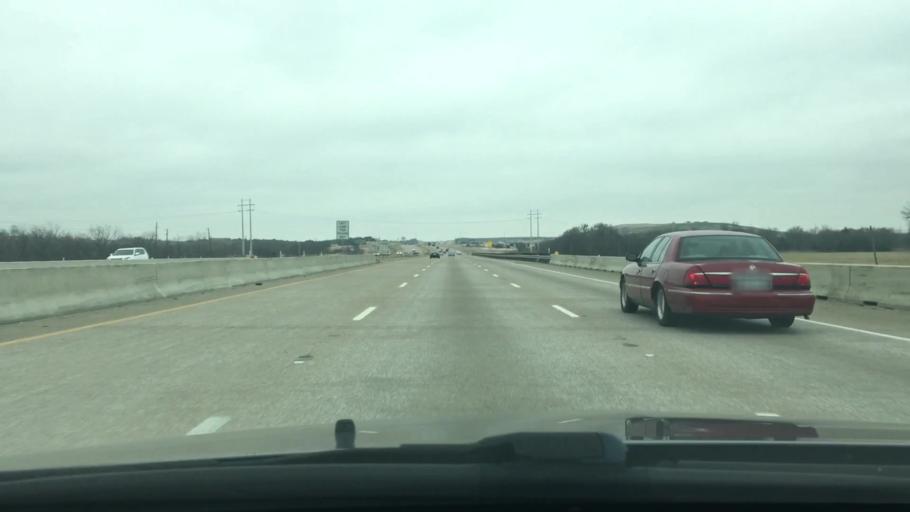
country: US
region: Texas
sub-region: Ellis County
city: Palmer
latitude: 32.4084
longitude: -96.6583
